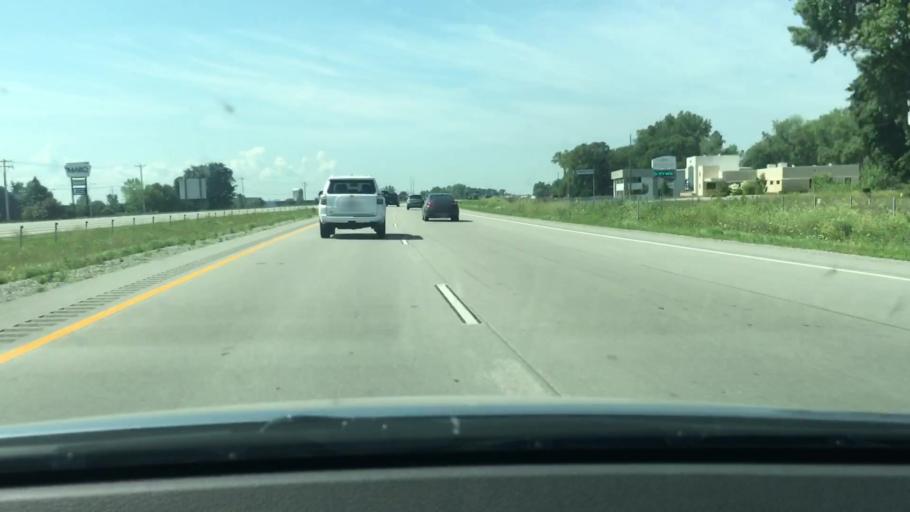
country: US
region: Wisconsin
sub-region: Brown County
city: Wrightstown
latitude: 44.3815
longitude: -88.1653
